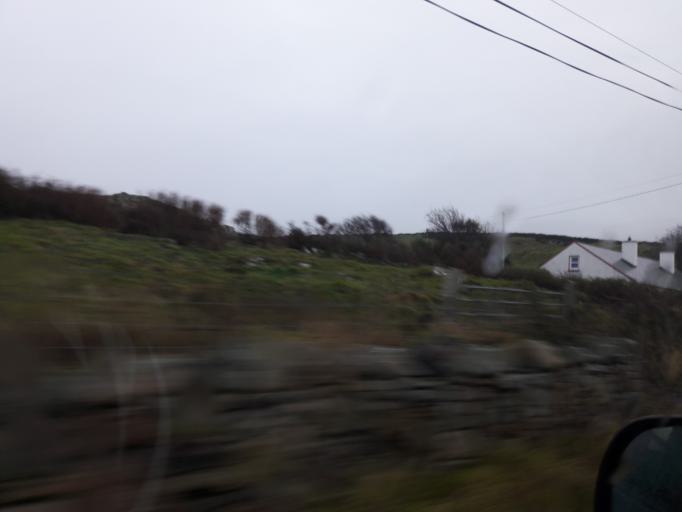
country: IE
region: Ulster
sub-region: County Donegal
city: Ramelton
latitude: 55.2645
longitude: -7.6612
